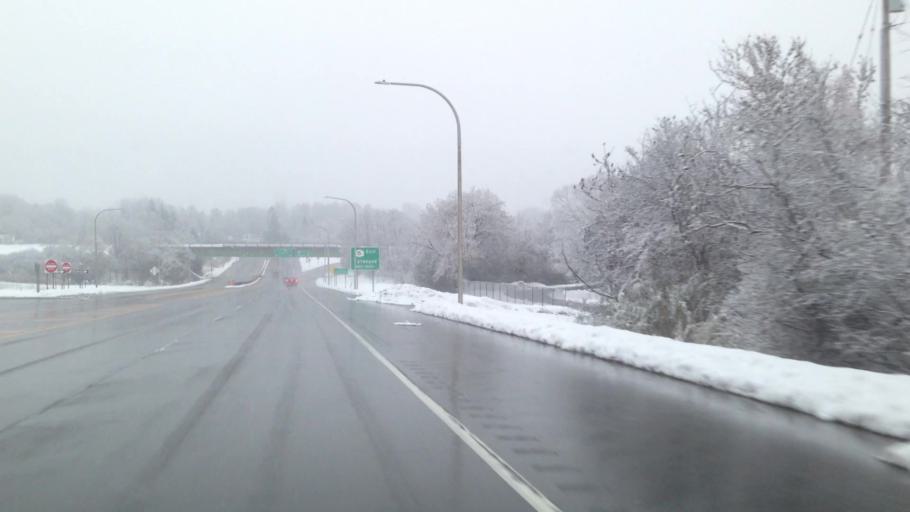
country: US
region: New York
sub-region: Onondaga County
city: Camillus
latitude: 43.0362
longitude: -76.3257
